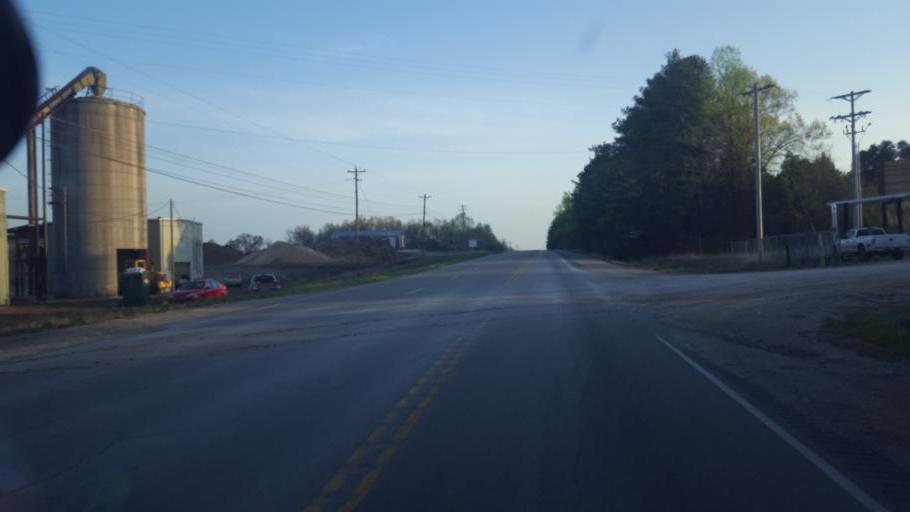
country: US
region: Kentucky
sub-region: Hart County
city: Munfordville
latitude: 37.3207
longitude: -85.9095
